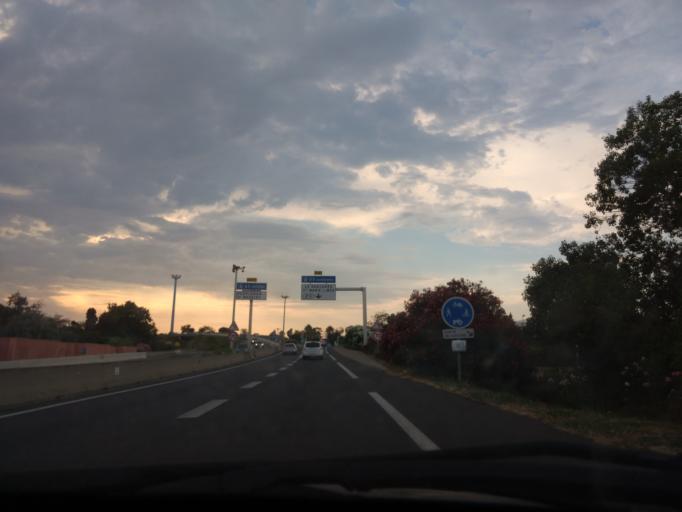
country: FR
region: Languedoc-Roussillon
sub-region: Departement des Pyrenees-Orientales
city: Canet-en-Roussillon
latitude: 42.7012
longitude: 3.0182
